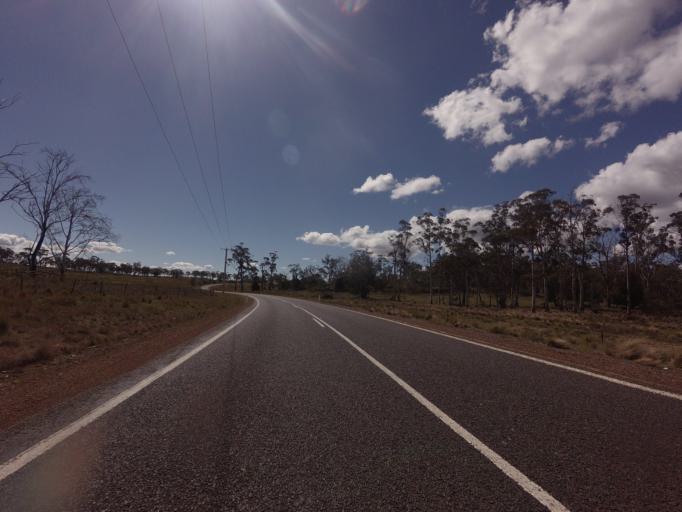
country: AU
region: Tasmania
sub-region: Northern Midlands
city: Evandale
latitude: -41.9526
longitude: 147.6107
